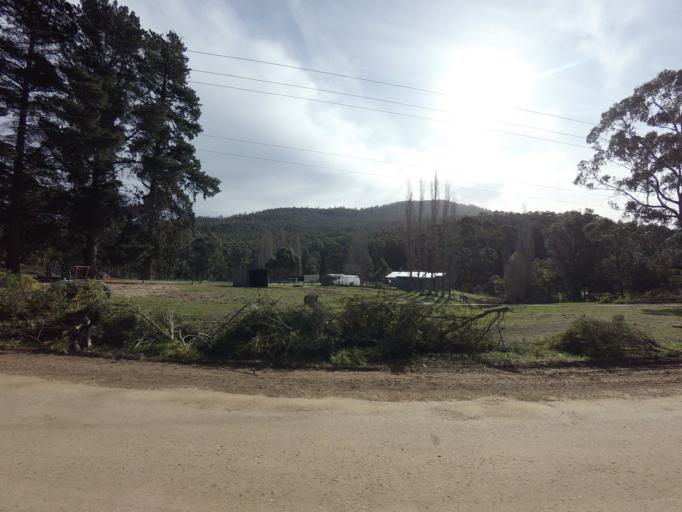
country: AU
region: Tasmania
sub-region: Huon Valley
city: Huonville
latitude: -43.0758
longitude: 147.0707
